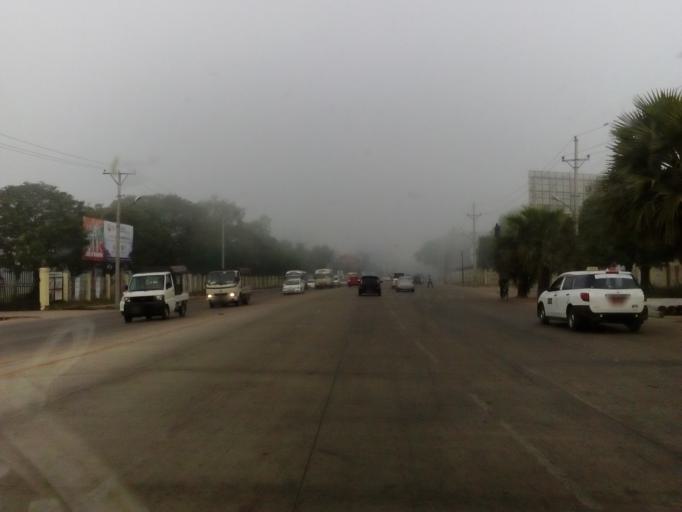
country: MM
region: Yangon
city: Yangon
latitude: 16.8198
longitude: 96.1850
